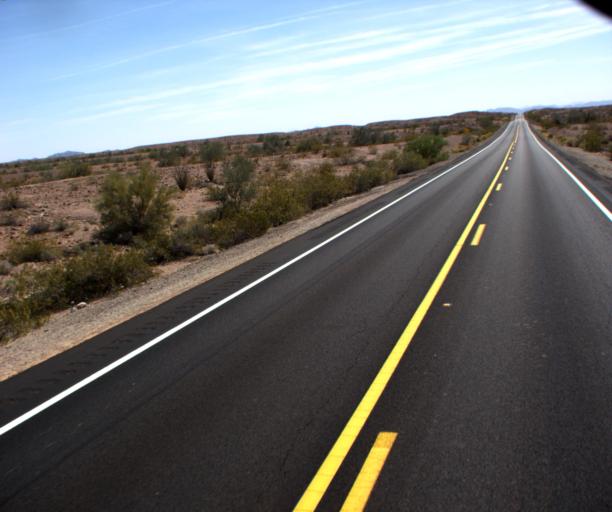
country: US
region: Arizona
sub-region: Yuma County
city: Wellton
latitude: 33.0892
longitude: -114.2969
